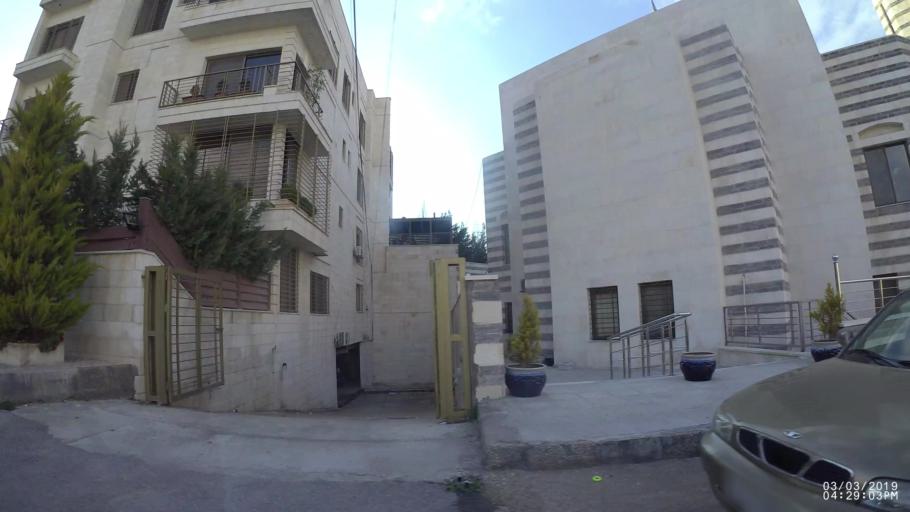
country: JO
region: Amman
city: Al Jubayhah
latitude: 31.9751
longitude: 35.8858
